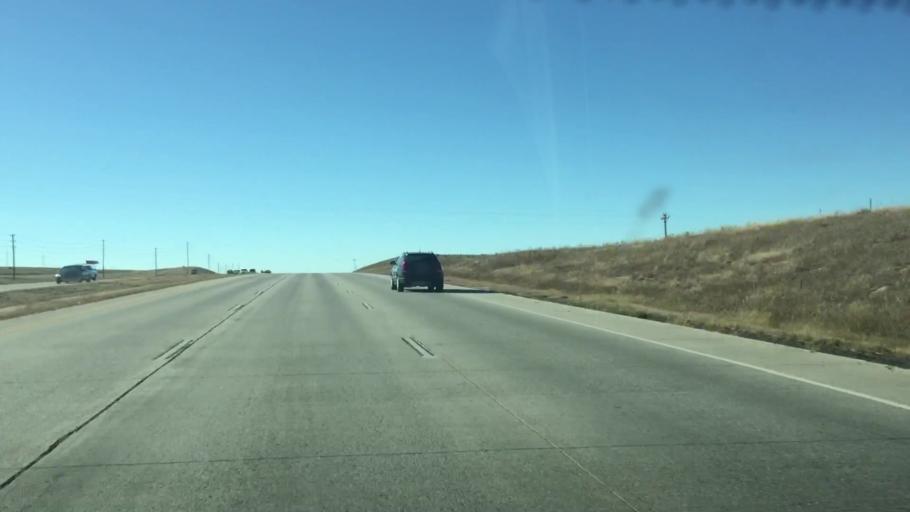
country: US
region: Colorado
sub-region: Douglas County
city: The Pinery
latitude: 39.4721
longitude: -104.7586
